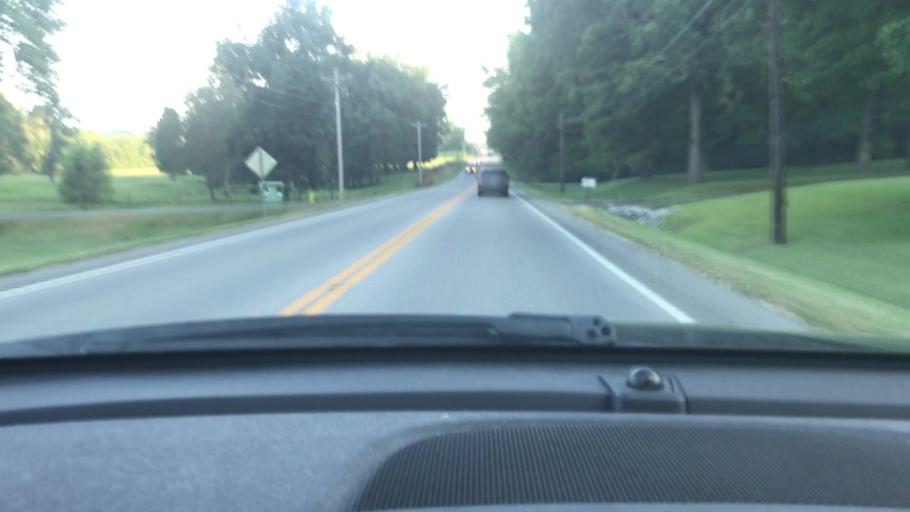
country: US
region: Tennessee
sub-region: Dickson County
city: Dickson
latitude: 36.1001
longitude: -87.3747
